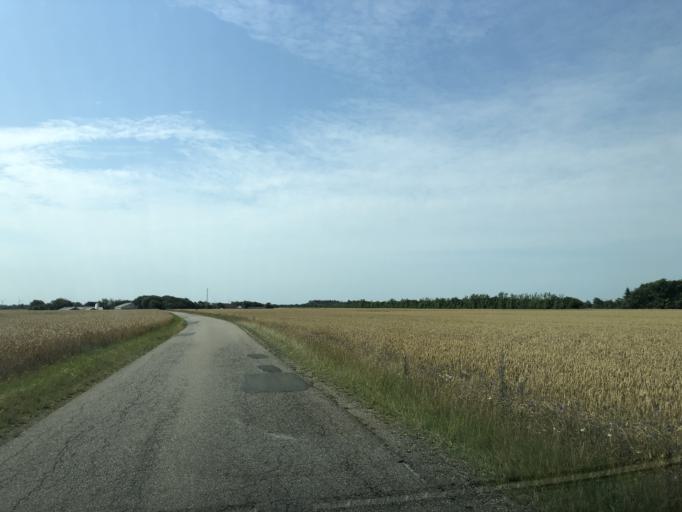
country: DK
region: Central Jutland
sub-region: Lemvig Kommune
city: Lemvig
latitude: 56.4440
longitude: 8.2898
